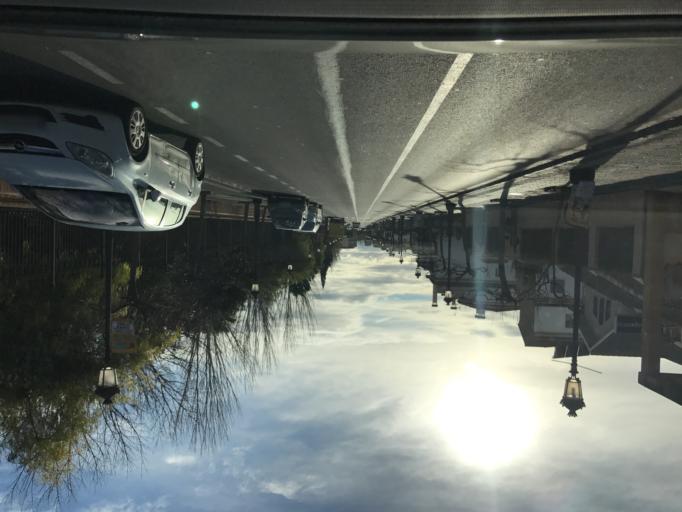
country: ES
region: Andalusia
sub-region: Provincia de Granada
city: Atarfe
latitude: 37.2205
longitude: -3.6869
